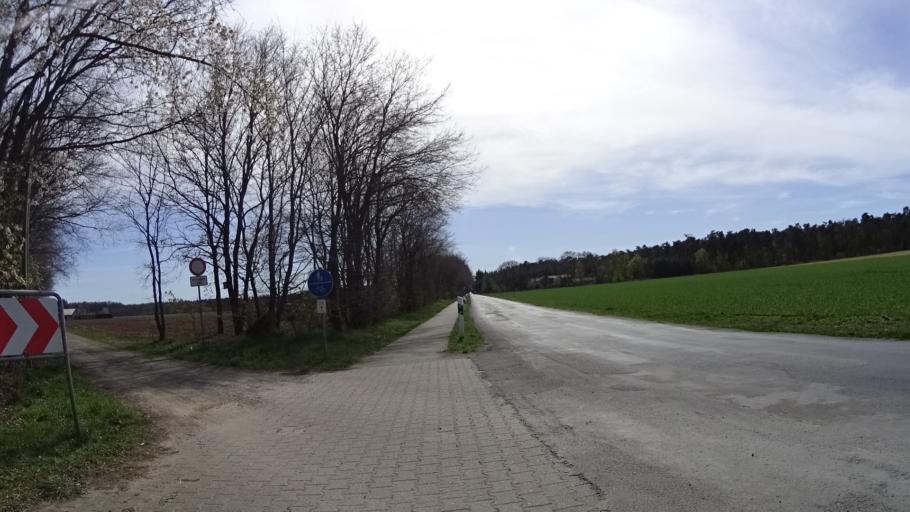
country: DE
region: Lower Saxony
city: Spelle
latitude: 52.3540
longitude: 7.4448
